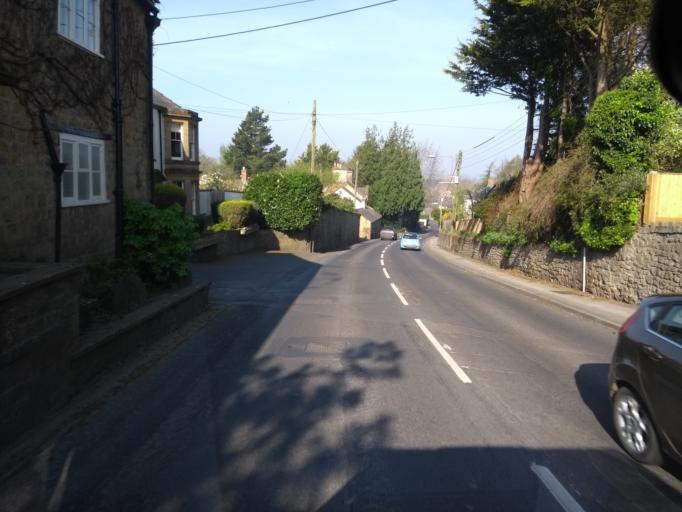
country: GB
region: England
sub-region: Somerset
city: Ilminster
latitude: 50.9288
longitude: -2.9185
